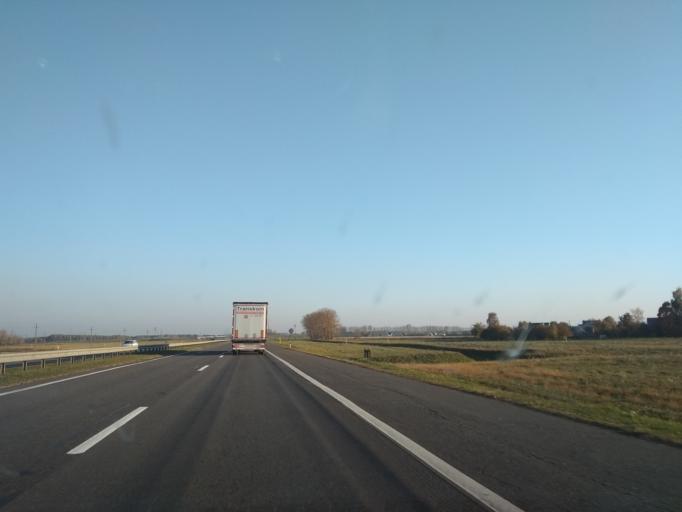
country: BY
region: Brest
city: Kobryn
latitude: 52.1897
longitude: 24.3125
